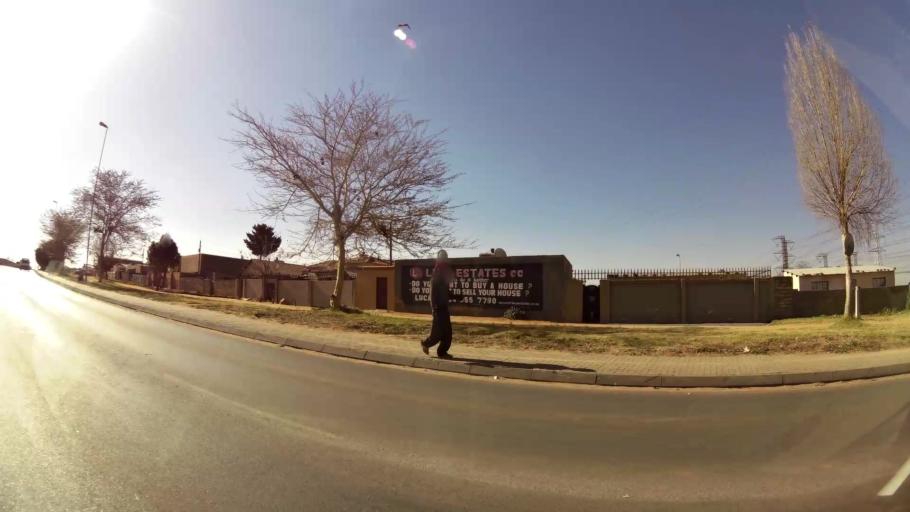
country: ZA
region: Gauteng
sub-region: Ekurhuleni Metropolitan Municipality
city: Tembisa
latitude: -26.0246
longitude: 28.2301
